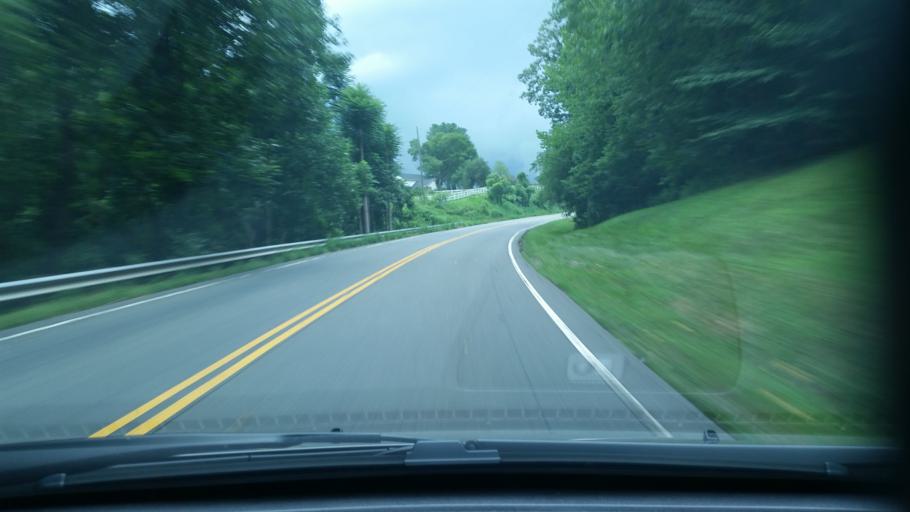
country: US
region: Virginia
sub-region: Nelson County
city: Nellysford
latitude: 37.8775
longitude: -78.8215
